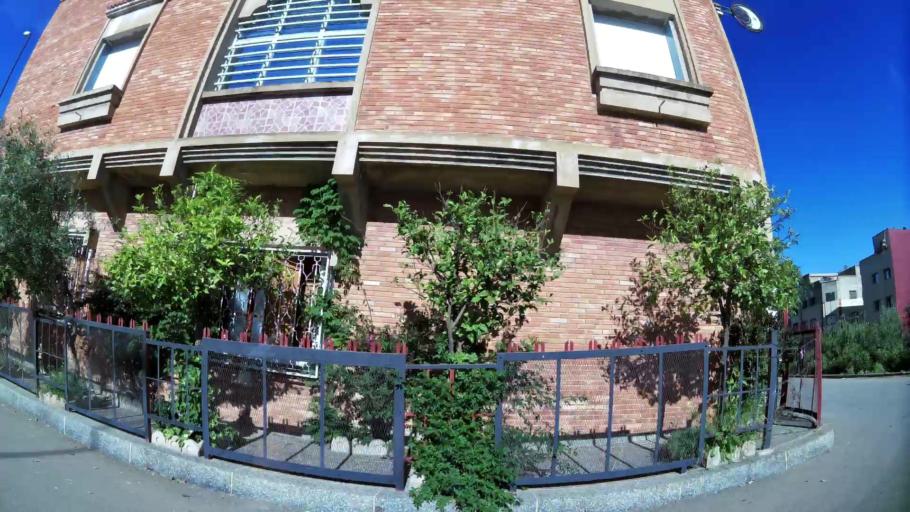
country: MA
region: Meknes-Tafilalet
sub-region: Meknes
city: Meknes
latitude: 33.8873
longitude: -5.5031
